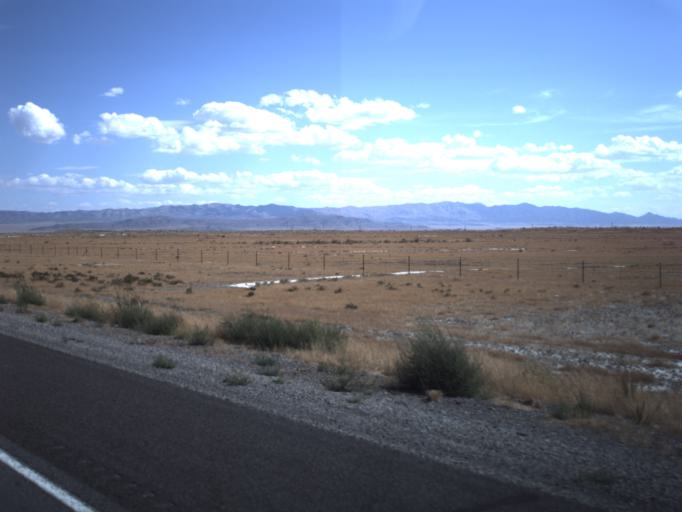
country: US
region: Utah
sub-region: Tooele County
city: Grantsville
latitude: 40.7259
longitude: -113.2113
